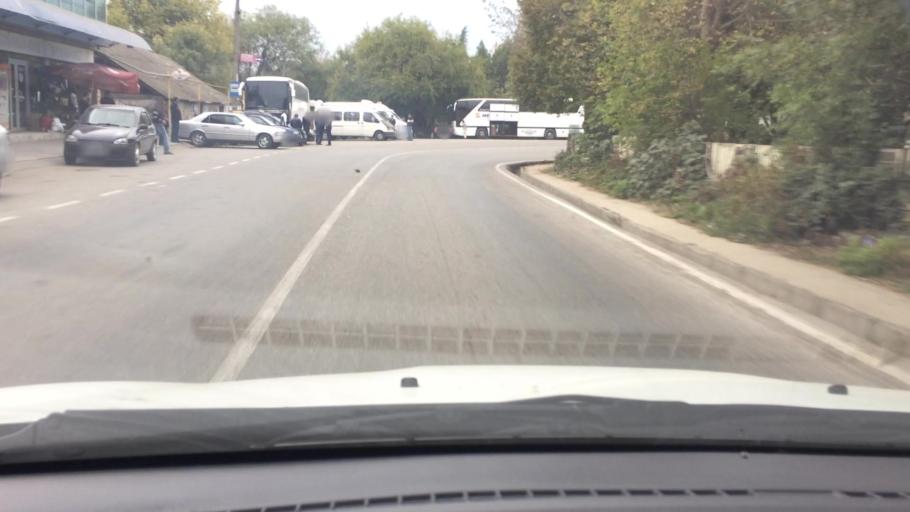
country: AM
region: Tavush
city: Bagratashen
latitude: 41.2467
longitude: 44.7991
